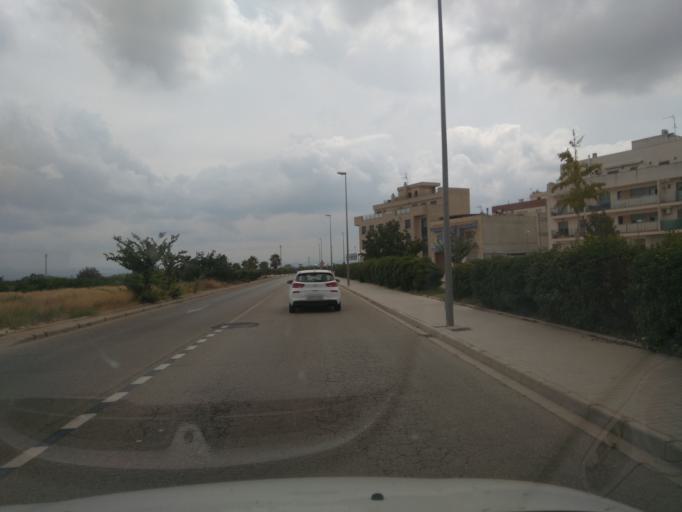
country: ES
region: Valencia
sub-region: Provincia de Valencia
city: L'Alcudia
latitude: 39.1930
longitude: -0.4991
